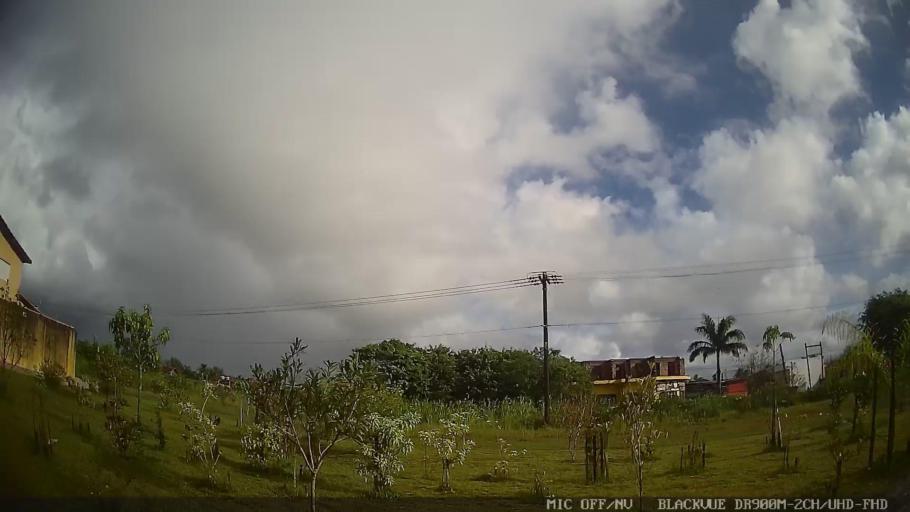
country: BR
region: Sao Paulo
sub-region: Itanhaem
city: Itanhaem
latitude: -24.2384
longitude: -46.8980
